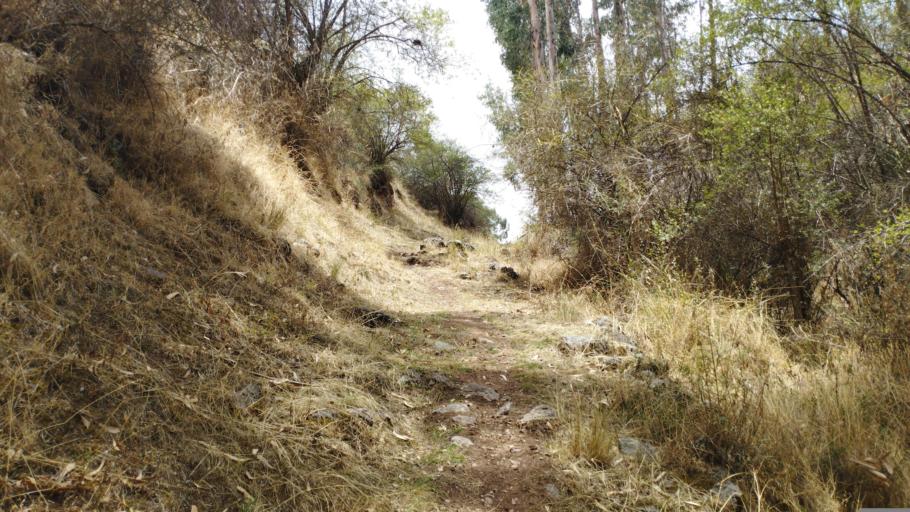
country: PE
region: Cusco
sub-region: Provincia de Cusco
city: Cusco
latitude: -13.5175
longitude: -71.9434
